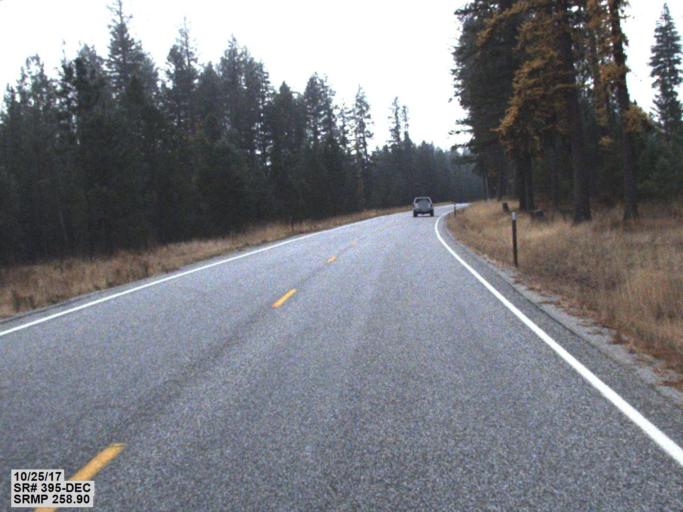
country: US
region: Washington
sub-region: Stevens County
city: Kettle Falls
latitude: 48.8474
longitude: -118.1998
